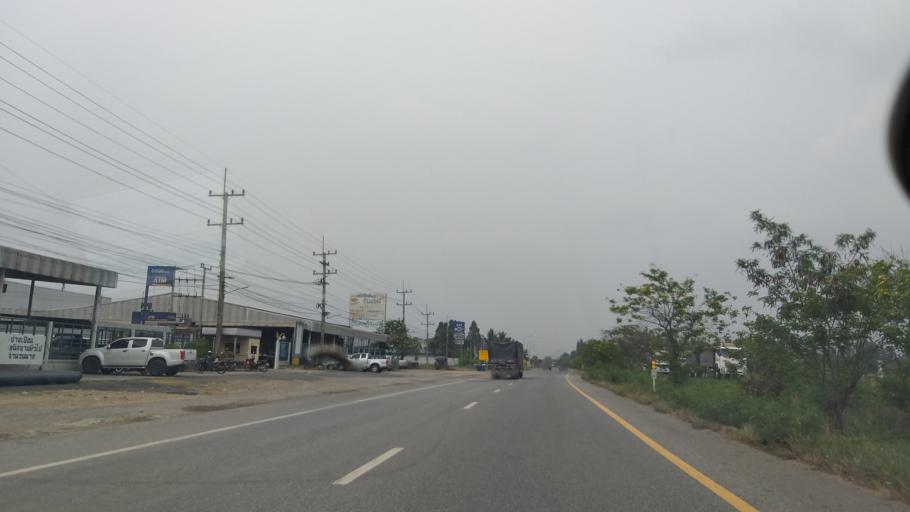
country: TH
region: Chon Buri
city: Ban Bueng
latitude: 13.2756
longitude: 101.2531
